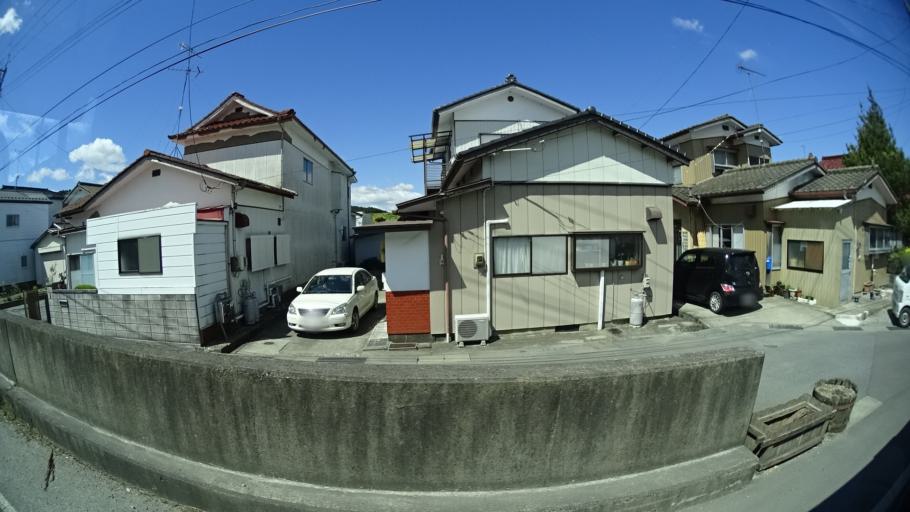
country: JP
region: Miyagi
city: Wakuya
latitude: 38.6045
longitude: 141.3007
